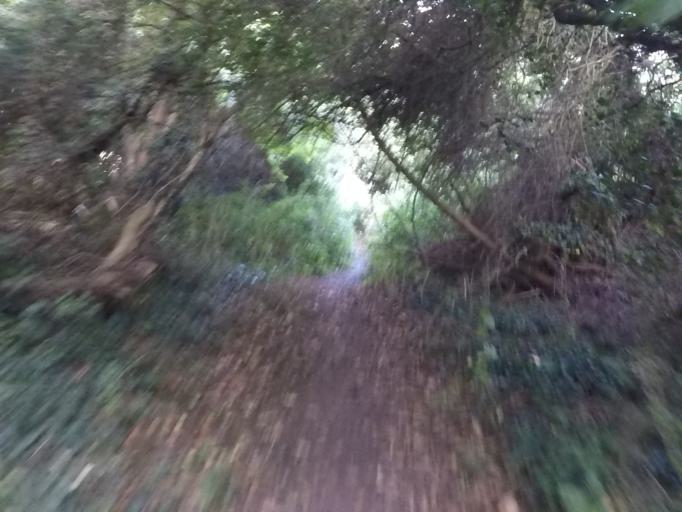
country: GB
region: England
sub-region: Oxfordshire
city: Charlbury
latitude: 51.8978
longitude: -1.4988
